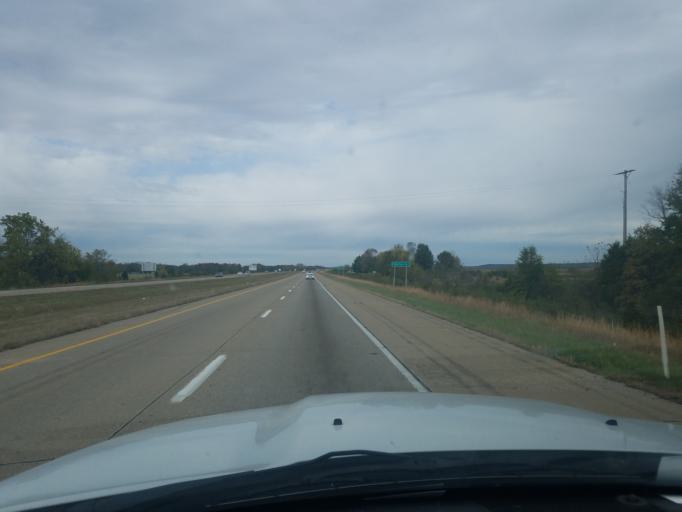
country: US
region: Indiana
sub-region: Vanderburgh County
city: Melody Hill
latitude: 38.0343
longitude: -87.4730
